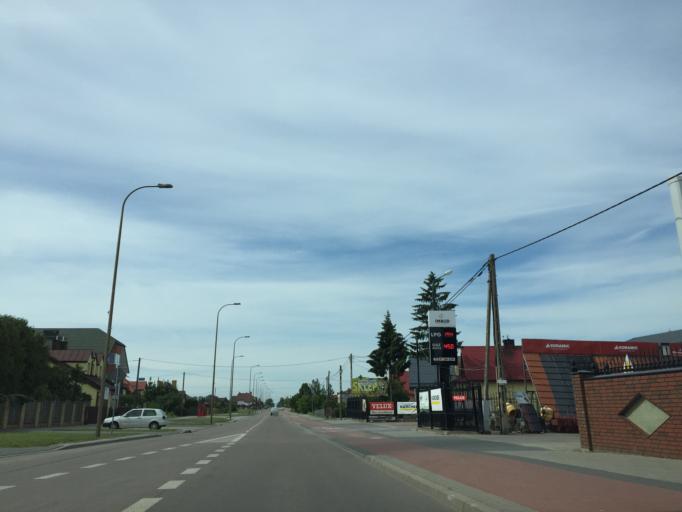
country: PL
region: Podlasie
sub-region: Suwalki
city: Suwalki
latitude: 54.0798
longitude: 22.9185
